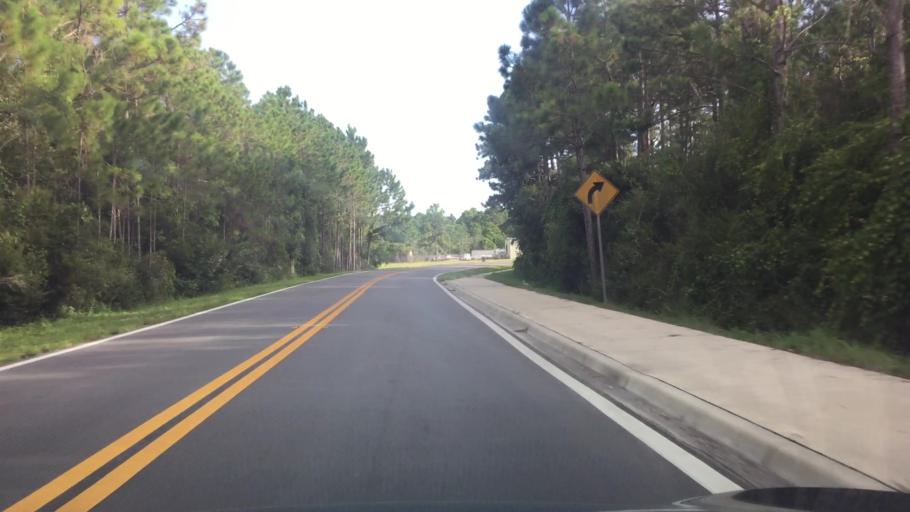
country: US
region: Florida
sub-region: Bay County
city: Panama City Beach
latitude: 30.2004
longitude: -85.8284
